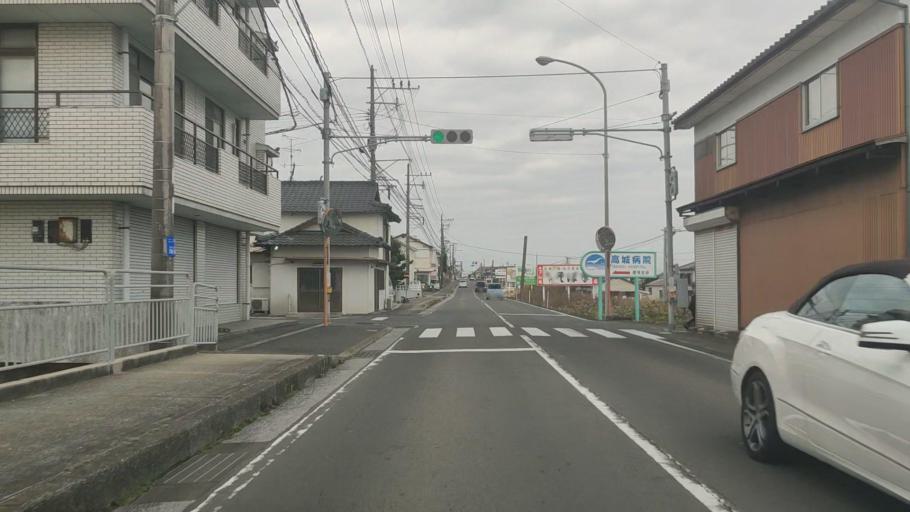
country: JP
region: Nagasaki
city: Shimabara
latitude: 32.8246
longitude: 130.3521
